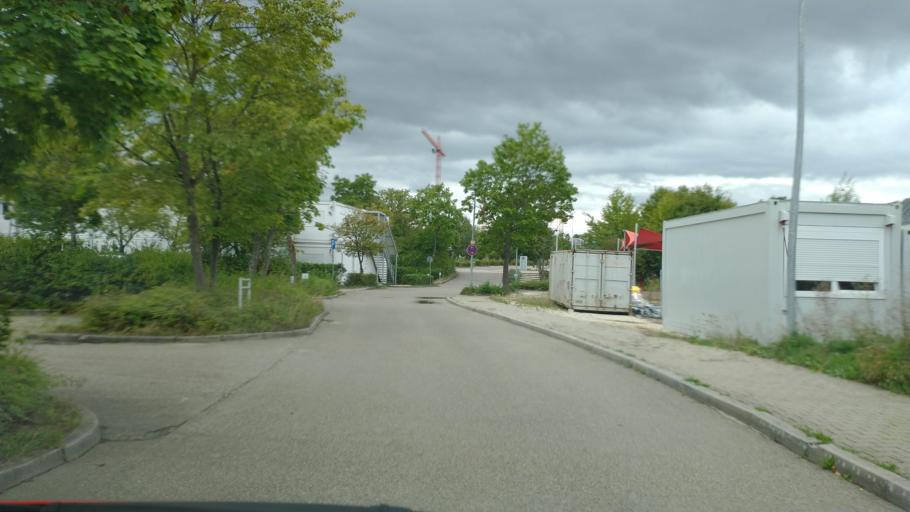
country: DE
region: Baden-Wuerttemberg
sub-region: Regierungsbezirk Stuttgart
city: Waldstetten
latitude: 48.7938
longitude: 9.8273
